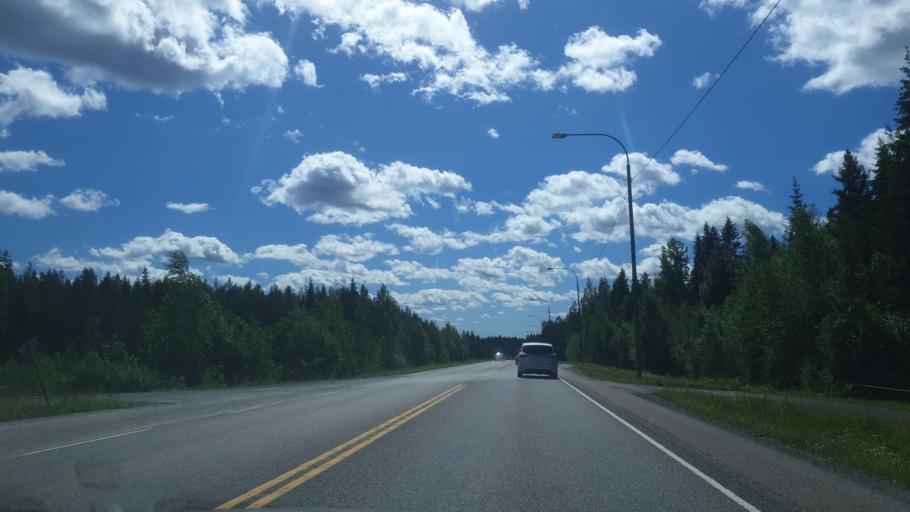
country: FI
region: Northern Savo
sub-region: Varkaus
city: Varkaus
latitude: 62.3684
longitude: 27.8098
